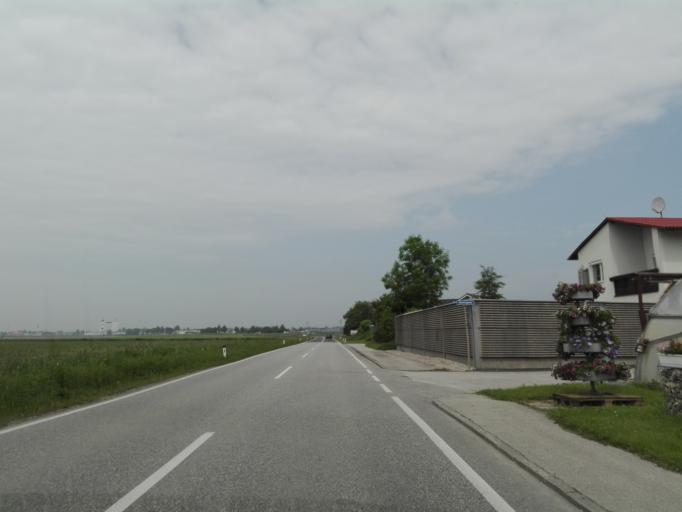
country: AT
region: Upper Austria
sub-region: Politischer Bezirk Urfahr-Umgebung
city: Goldworth
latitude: 48.2875
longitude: 14.1400
